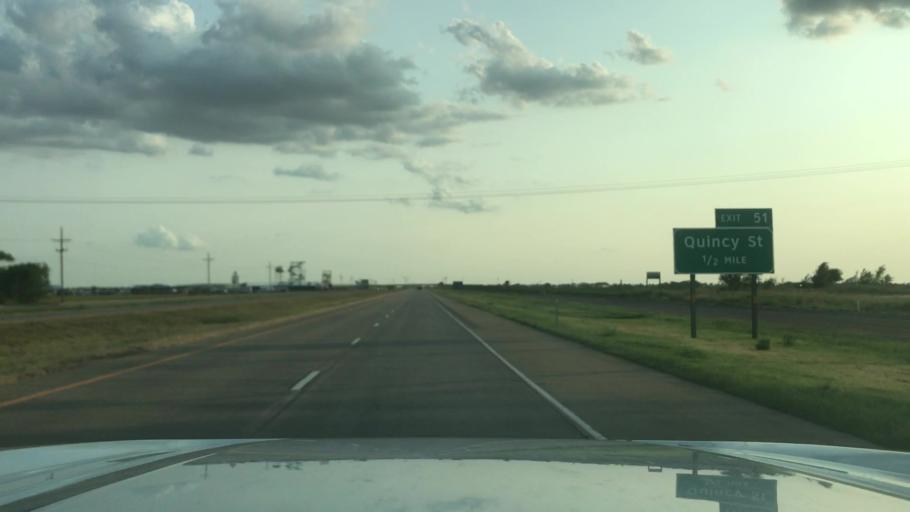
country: US
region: Texas
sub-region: Hale County
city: Seth Ward
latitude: 34.2276
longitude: -101.7160
